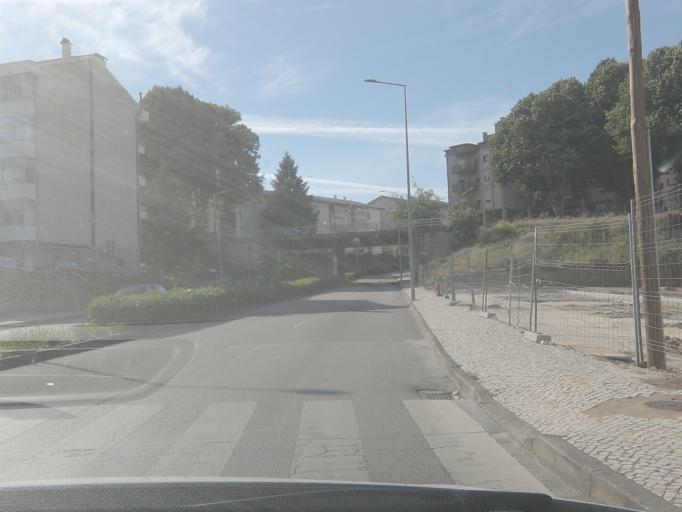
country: PT
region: Viseu
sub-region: Viseu
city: Viseu
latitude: 40.6496
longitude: -7.9094
